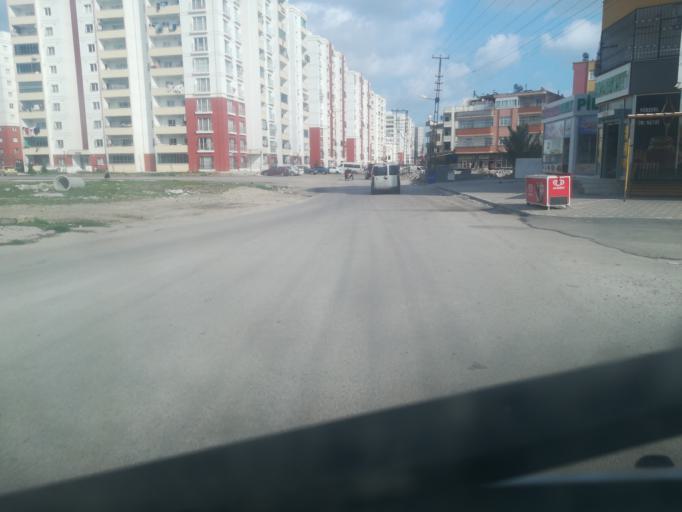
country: TR
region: Adana
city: Seyhan
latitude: 37.0085
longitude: 35.2740
